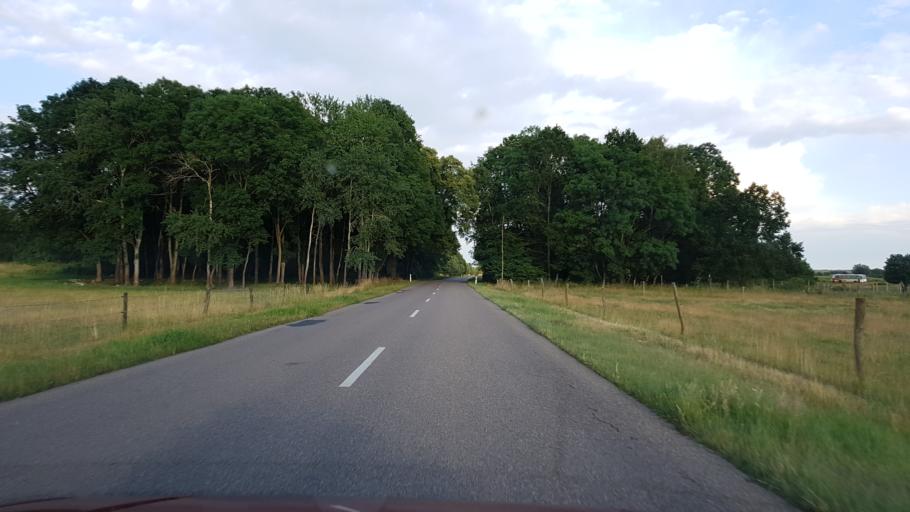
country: PL
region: West Pomeranian Voivodeship
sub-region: Powiat goleniowski
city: Nowogard
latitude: 53.6951
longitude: 15.0629
